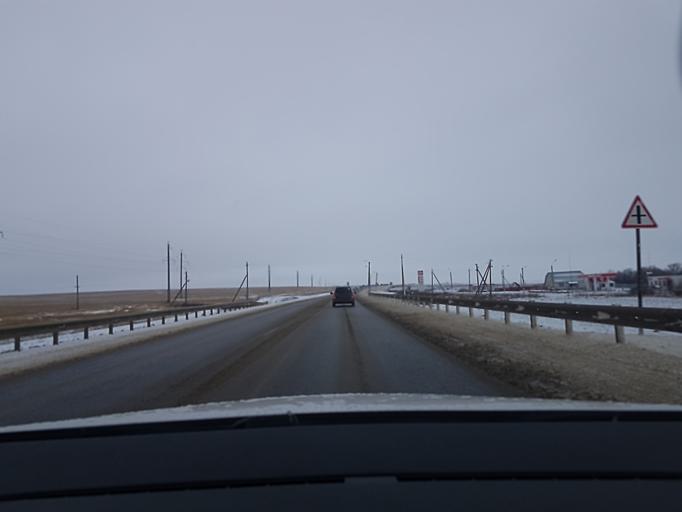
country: RU
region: Rjazan
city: Vilenka
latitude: 54.3340
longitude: 38.7988
